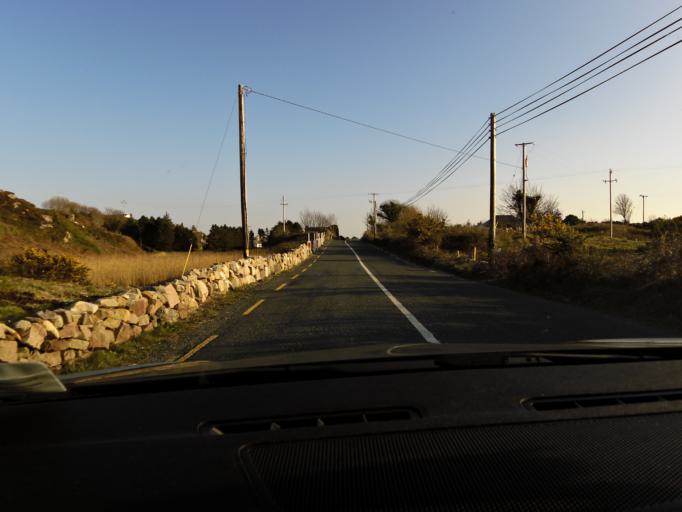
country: IE
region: Connaught
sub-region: County Galway
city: Oughterard
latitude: 53.2901
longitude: -9.5491
